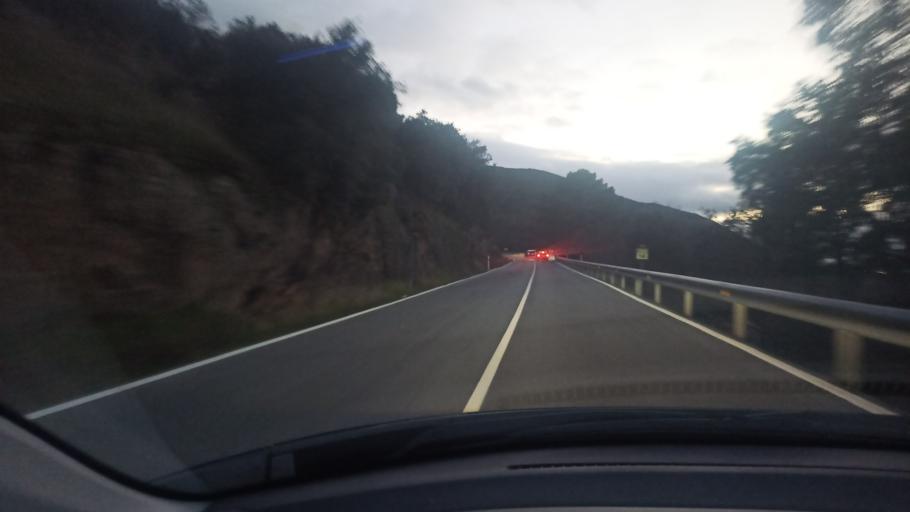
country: ES
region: Madrid
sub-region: Provincia de Madrid
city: Robledo de Chavela
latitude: 40.4687
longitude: -4.2606
